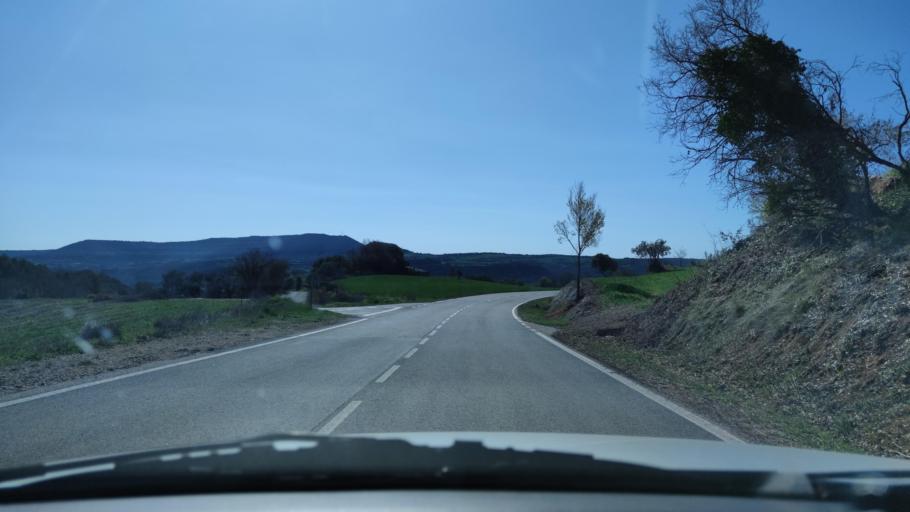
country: ES
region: Catalonia
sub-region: Provincia de Lleida
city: Artesa de Segre
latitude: 41.9296
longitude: 1.0554
